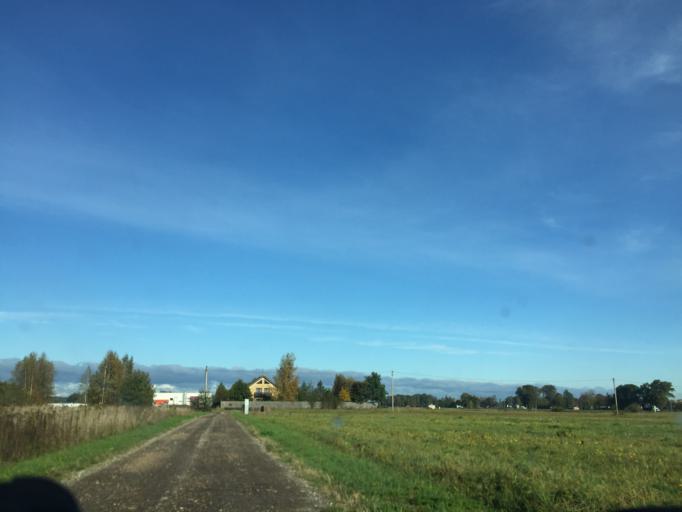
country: LV
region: Adazi
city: Adazi
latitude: 57.0921
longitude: 24.3082
